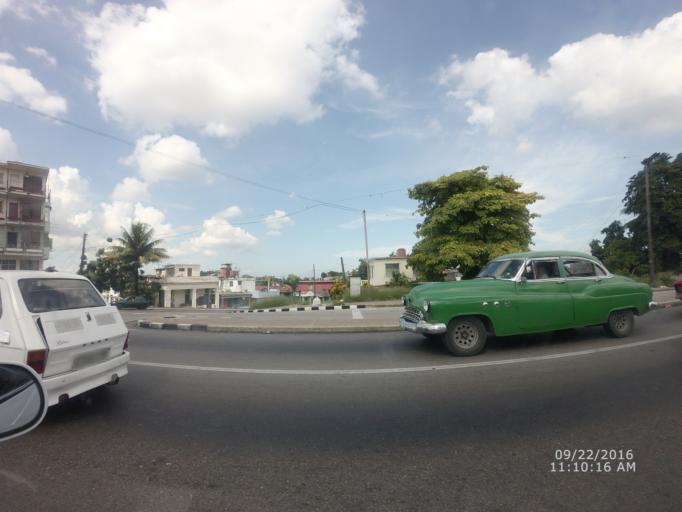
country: CU
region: La Habana
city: Cerro
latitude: 23.1022
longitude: -82.4203
